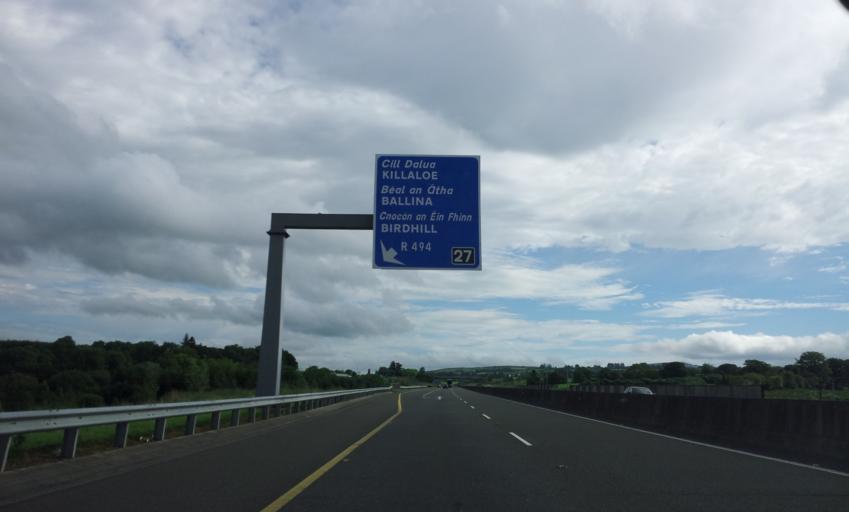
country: IE
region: Munster
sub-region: North Tipperary
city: Newport
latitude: 52.7534
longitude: -8.4182
